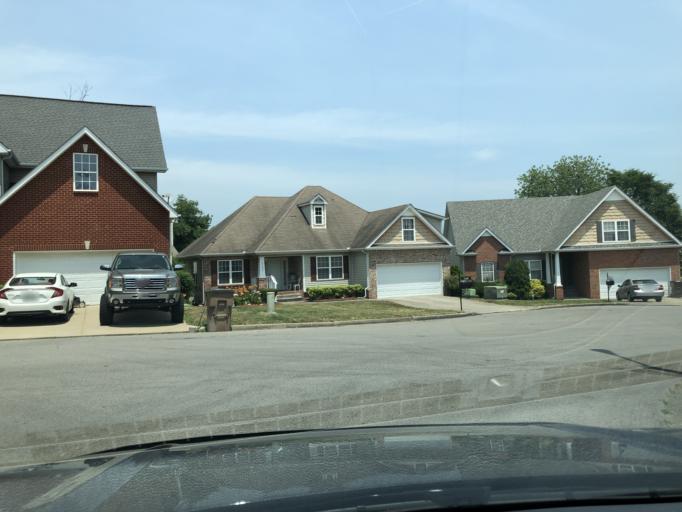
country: US
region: Tennessee
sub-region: Rutherford County
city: La Vergne
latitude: 36.0478
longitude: -86.6202
